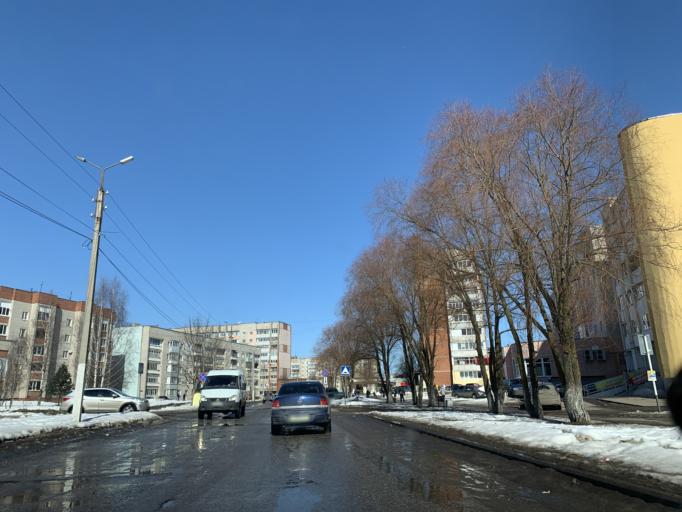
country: RU
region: Jaroslavl
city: Tutayev
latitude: 57.8618
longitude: 39.5108
